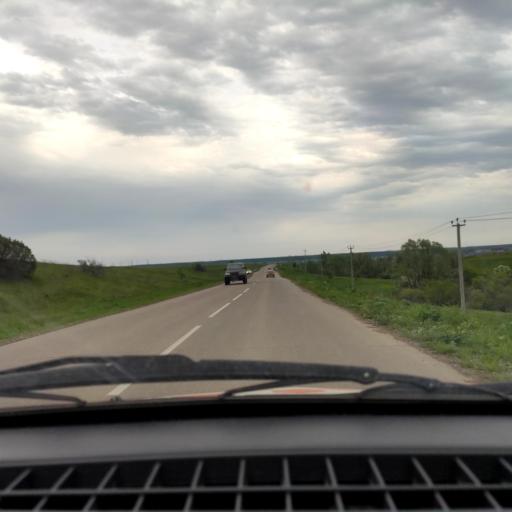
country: RU
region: Bashkortostan
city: Avdon
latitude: 54.5670
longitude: 55.7587
